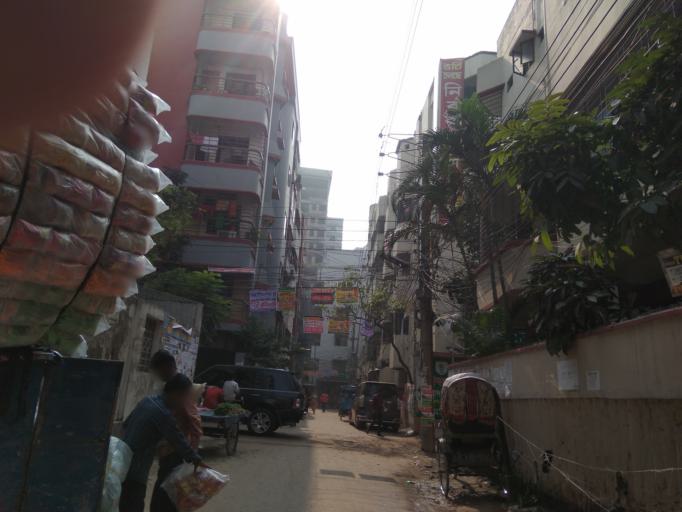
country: BD
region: Dhaka
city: Azimpur
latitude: 23.7665
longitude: 90.3570
